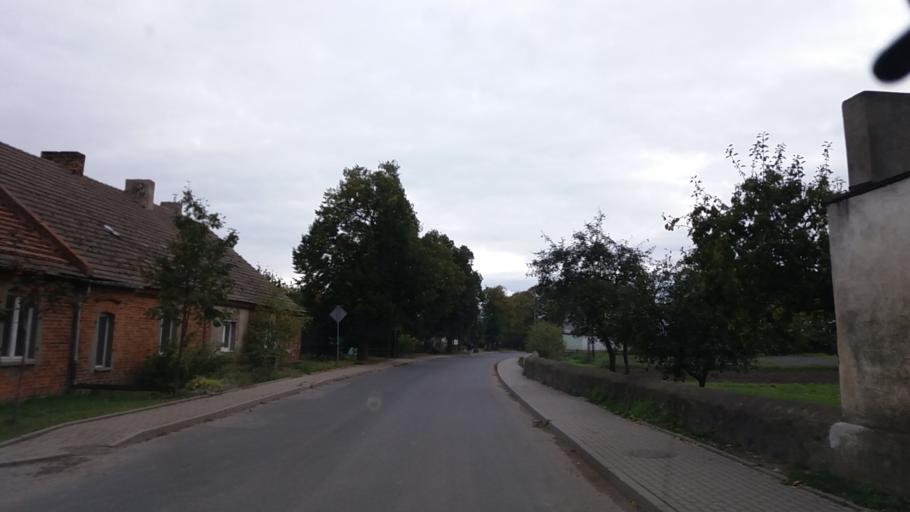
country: PL
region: West Pomeranian Voivodeship
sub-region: Powiat choszczenski
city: Pelczyce
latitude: 53.0238
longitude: 15.3667
